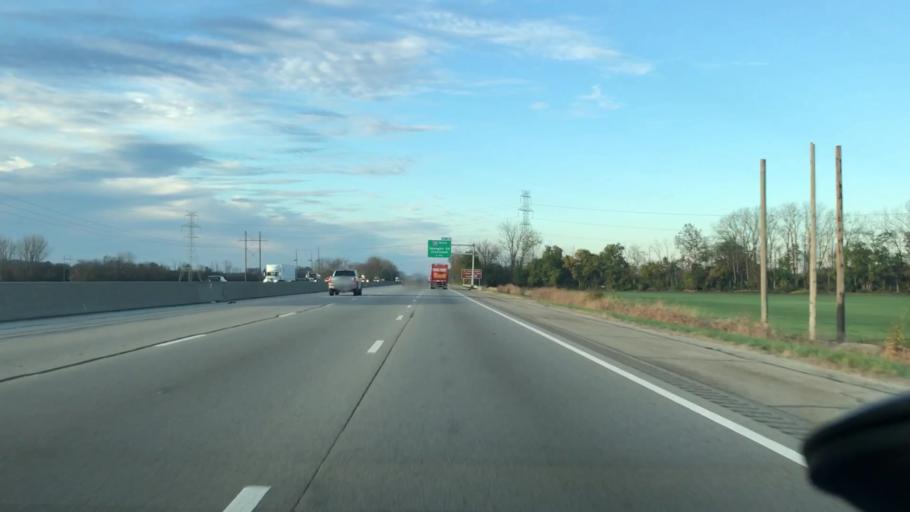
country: US
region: Ohio
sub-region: Clark County
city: Holiday Valley
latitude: 39.8749
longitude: -83.9707
